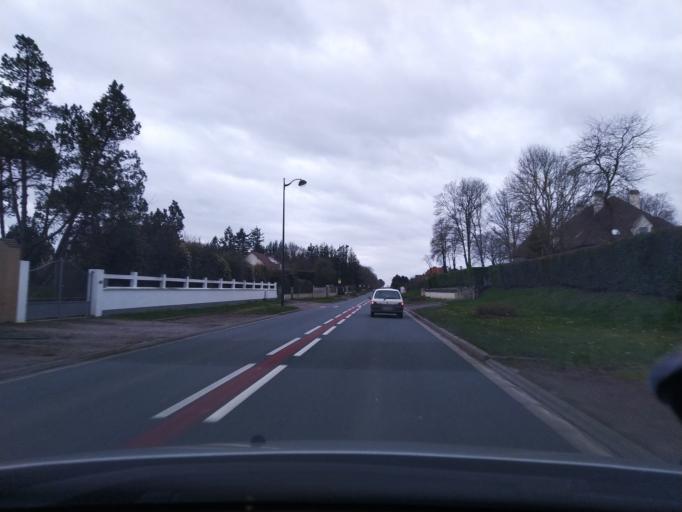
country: FR
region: Picardie
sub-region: Departement de la Somme
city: Abbeville
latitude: 50.1545
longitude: 1.8540
